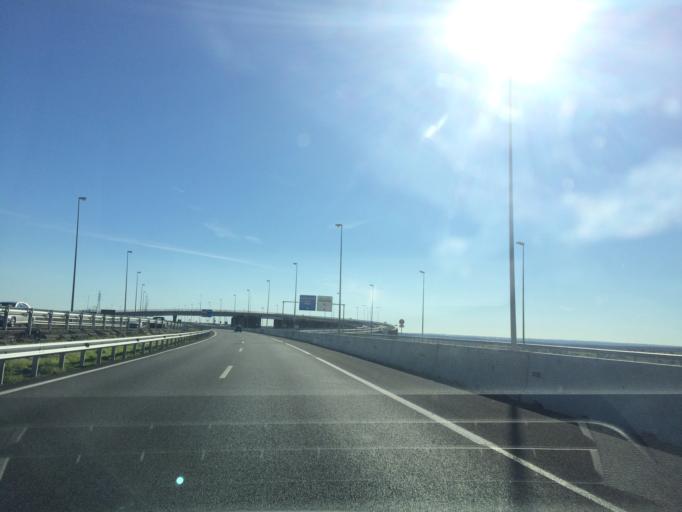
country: ES
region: Madrid
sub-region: Provincia de Madrid
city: Tres Cantos
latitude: 40.6232
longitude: -3.7303
